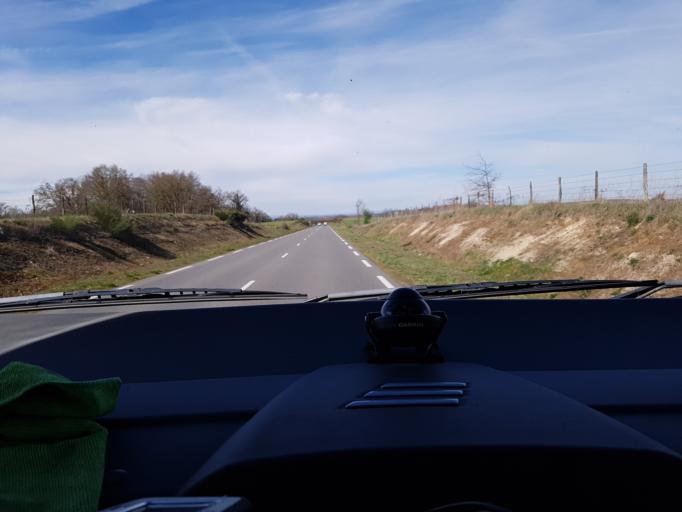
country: FR
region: Auvergne
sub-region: Departement de l'Allier
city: Lapalisse
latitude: 46.2285
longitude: 3.5847
